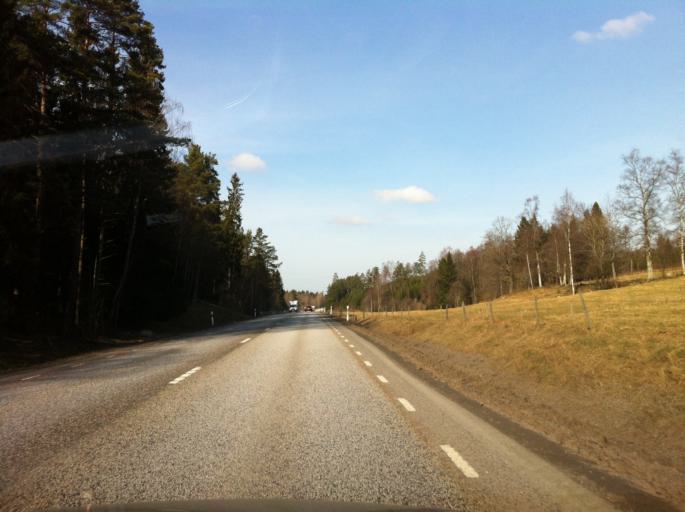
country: SE
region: Joenkoeping
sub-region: Mullsjo Kommun
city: Mullsjoe
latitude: 57.9474
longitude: 13.8368
